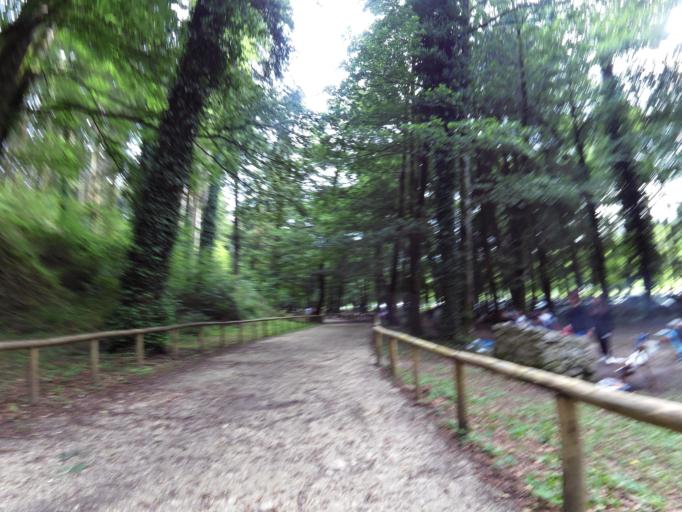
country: IT
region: Calabria
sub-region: Provincia di Vibo-Valentia
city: Serra San Bruno
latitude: 38.5578
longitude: 16.3148
